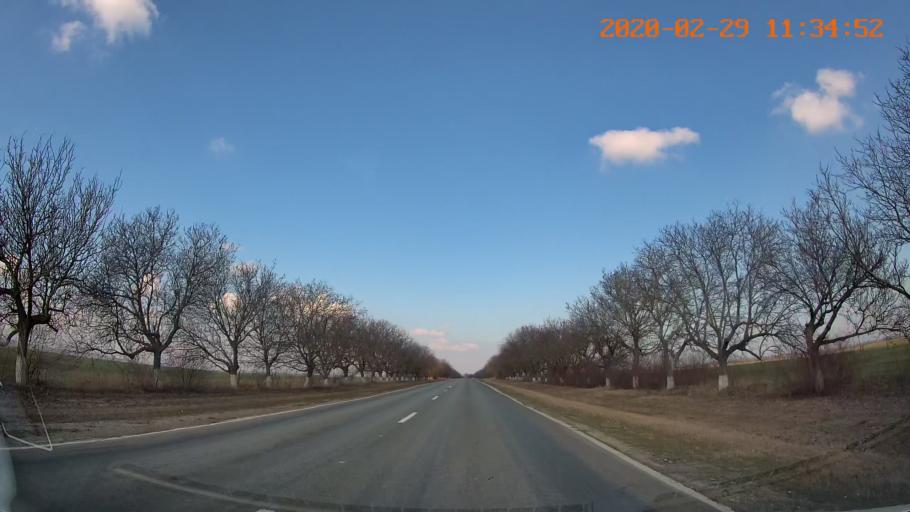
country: MD
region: Rezina
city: Saharna
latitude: 47.5718
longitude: 29.0692
